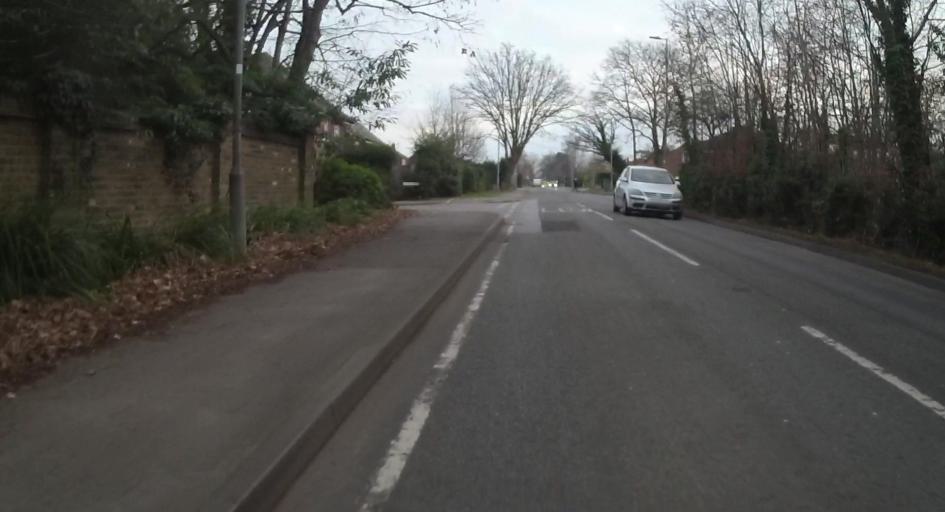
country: GB
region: England
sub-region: Bracknell Forest
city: Bracknell
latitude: 51.4256
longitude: -0.7645
